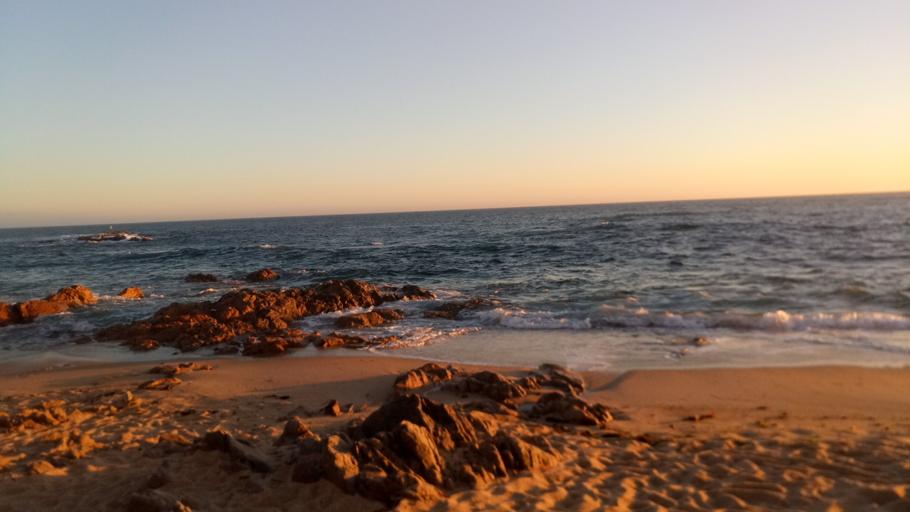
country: PT
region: Porto
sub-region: Povoa de Varzim
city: Aver-o-Mar
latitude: 41.3935
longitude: -8.7769
